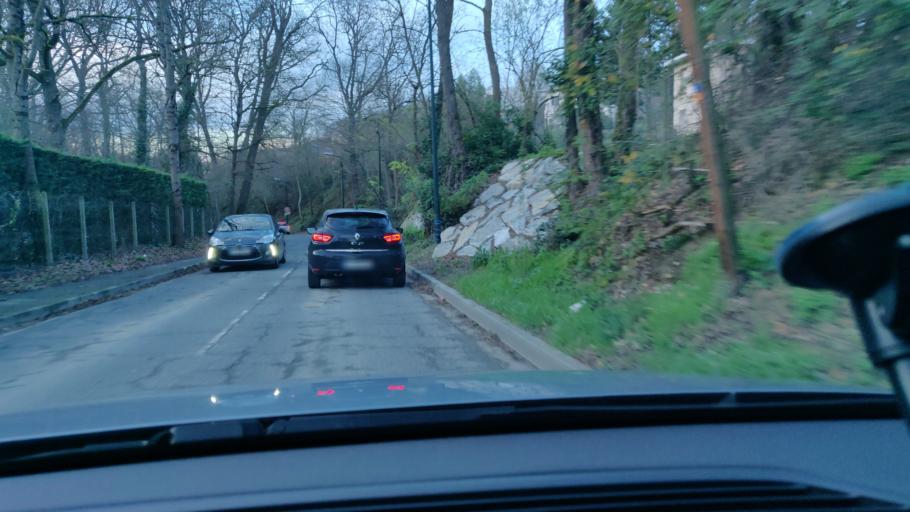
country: FR
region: Midi-Pyrenees
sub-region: Departement de la Haute-Garonne
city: Ramonville-Saint-Agne
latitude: 43.5480
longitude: 1.4507
